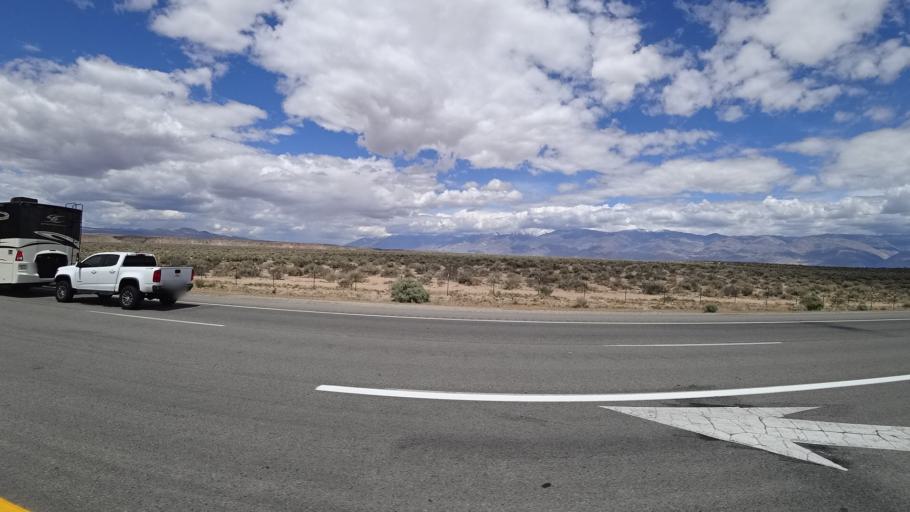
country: US
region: California
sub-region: Inyo County
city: West Bishop
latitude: 37.3815
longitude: -118.4792
